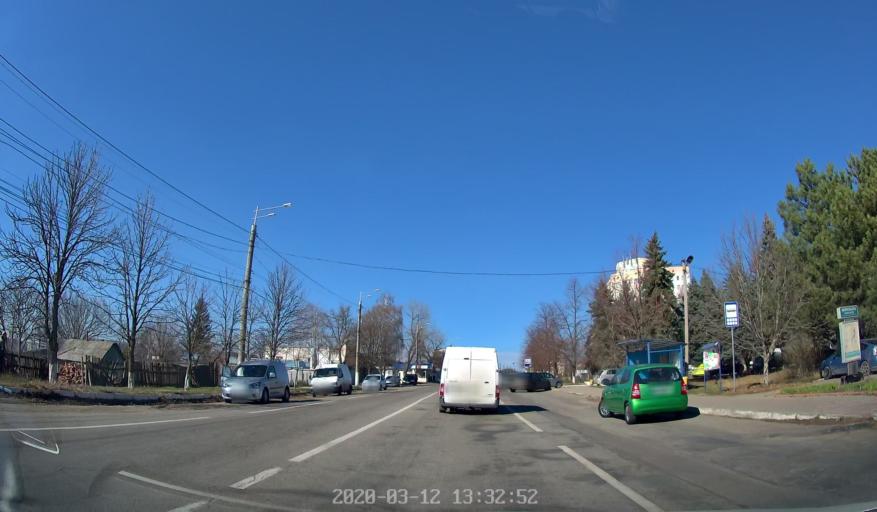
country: MD
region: Laloveni
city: Ialoveni
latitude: 46.9535
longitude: 28.7704
